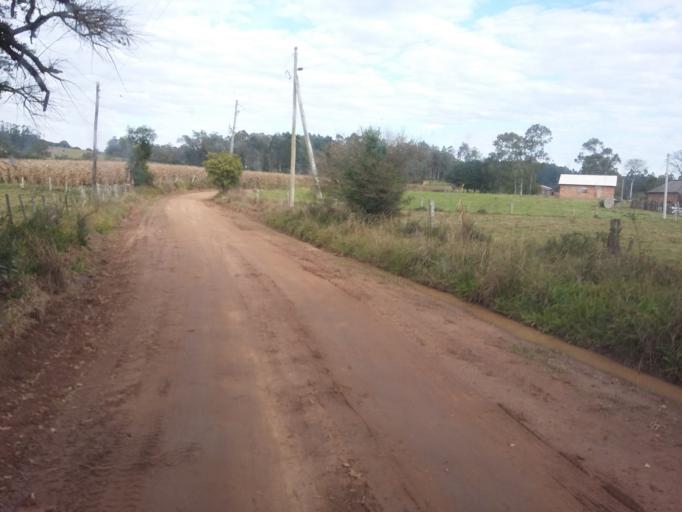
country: BR
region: Rio Grande do Sul
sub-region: Camaqua
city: Camaqua
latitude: -30.7130
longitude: -51.7826
